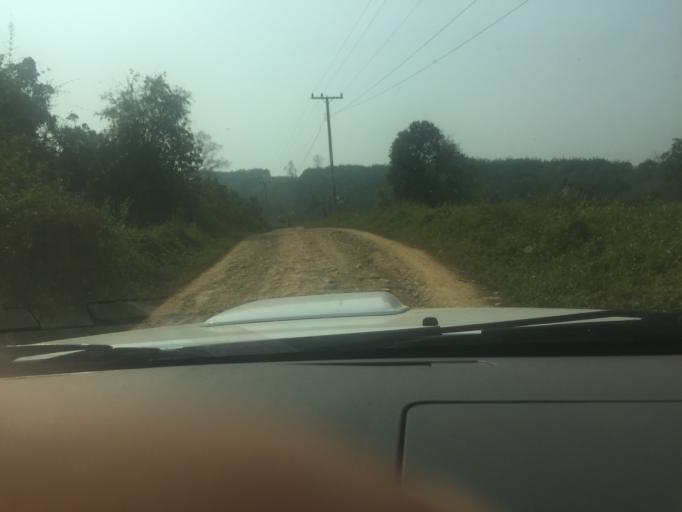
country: TH
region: Phayao
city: Phu Sang
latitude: 19.6301
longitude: 100.5365
